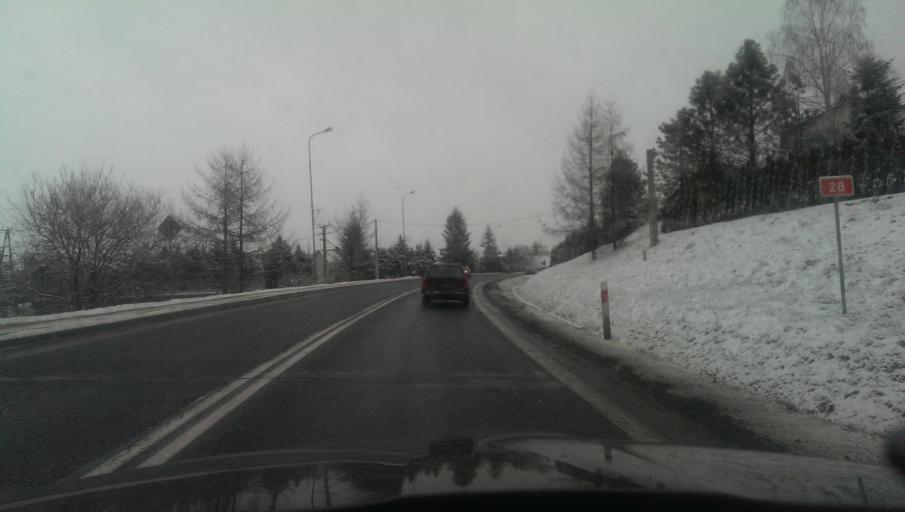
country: PL
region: Subcarpathian Voivodeship
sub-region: Powiat sanocki
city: Besko
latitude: 49.5880
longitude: 21.9476
